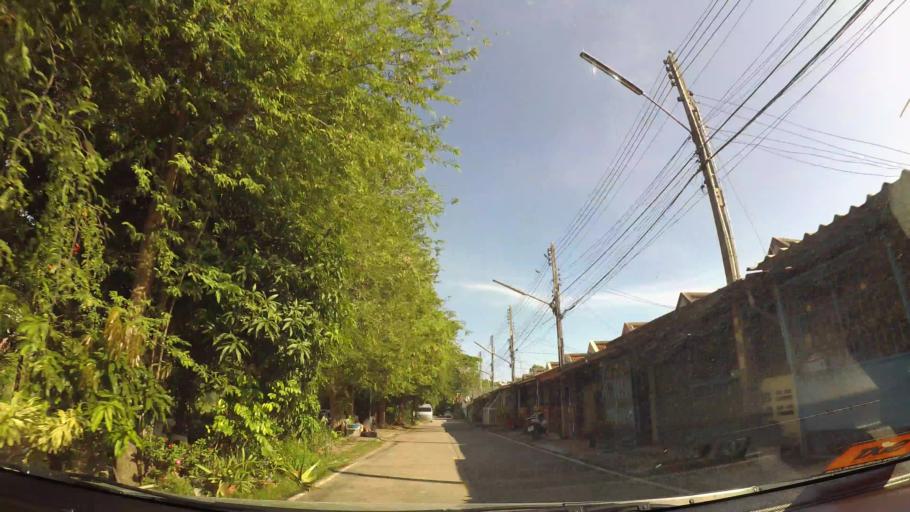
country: TH
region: Rayong
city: Rayong
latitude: 12.6711
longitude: 101.3018
